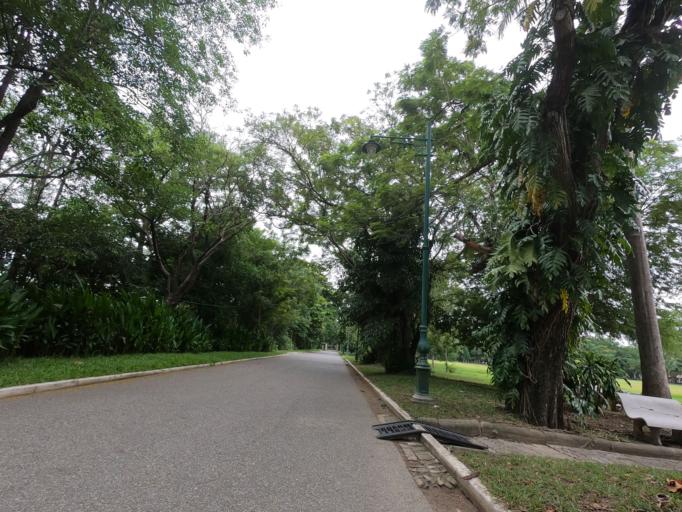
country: TH
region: Nakhon Pathom
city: Nakhon Pathom
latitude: 13.8207
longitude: 100.0476
